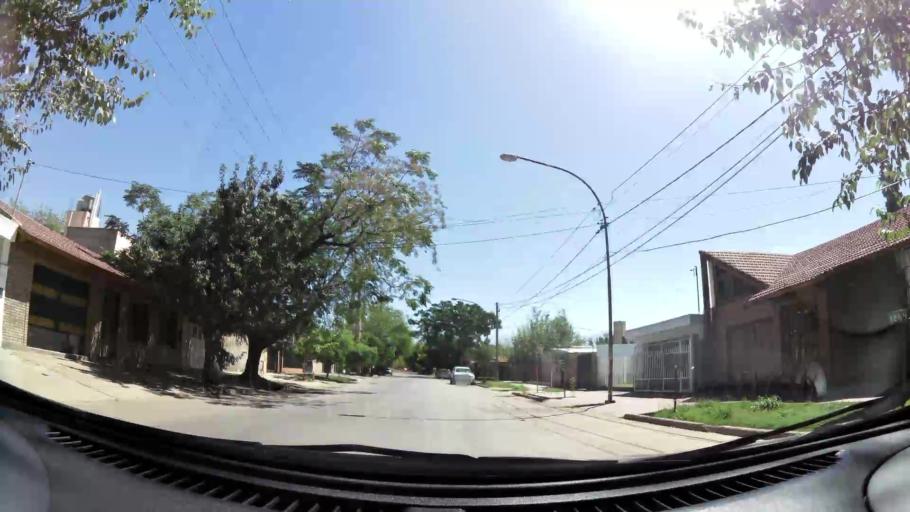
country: AR
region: Mendoza
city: Mendoza
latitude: -32.8789
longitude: -68.8067
